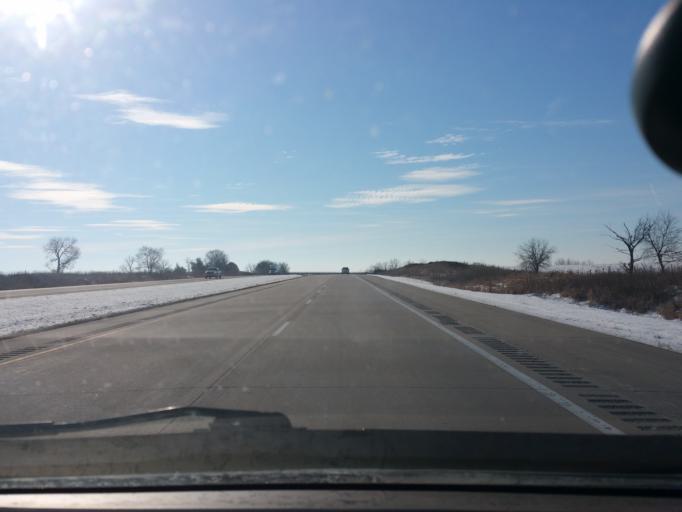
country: US
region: Iowa
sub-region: Clarke County
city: Osceola
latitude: 40.9190
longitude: -93.7973
